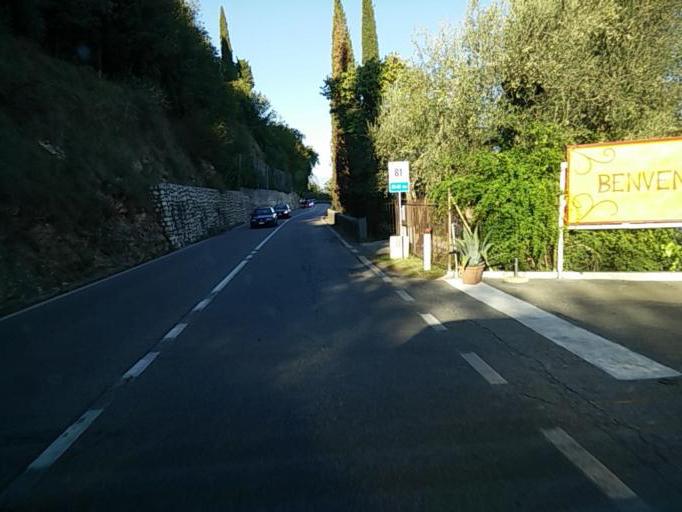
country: IT
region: Lombardy
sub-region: Provincia di Brescia
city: Gargnano
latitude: 45.6623
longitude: 10.6435
